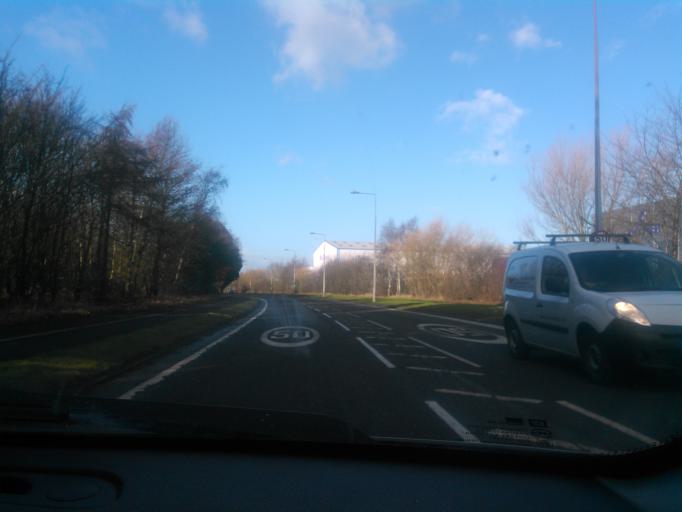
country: GB
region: England
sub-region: Shropshire
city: Hadley
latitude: 52.7143
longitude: -2.4719
